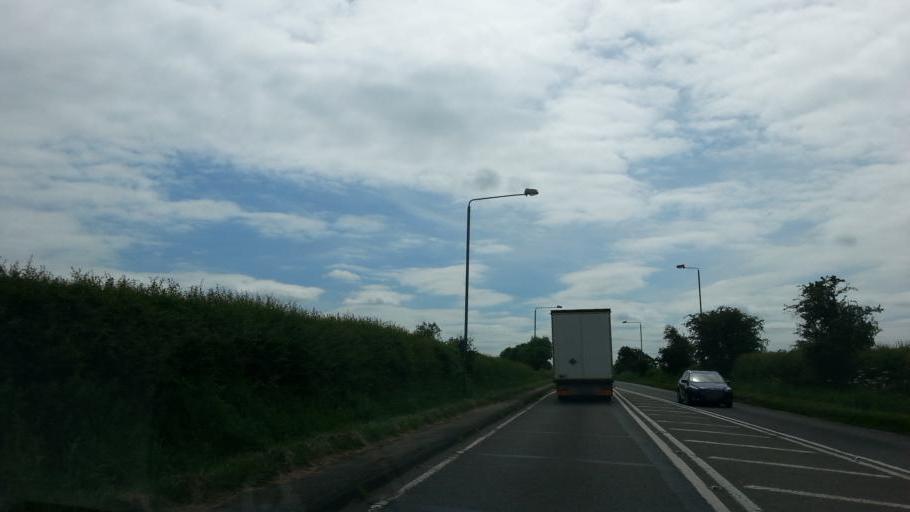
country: GB
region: England
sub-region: Nottinghamshire
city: Cotgrave
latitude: 52.8905
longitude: -1.0816
